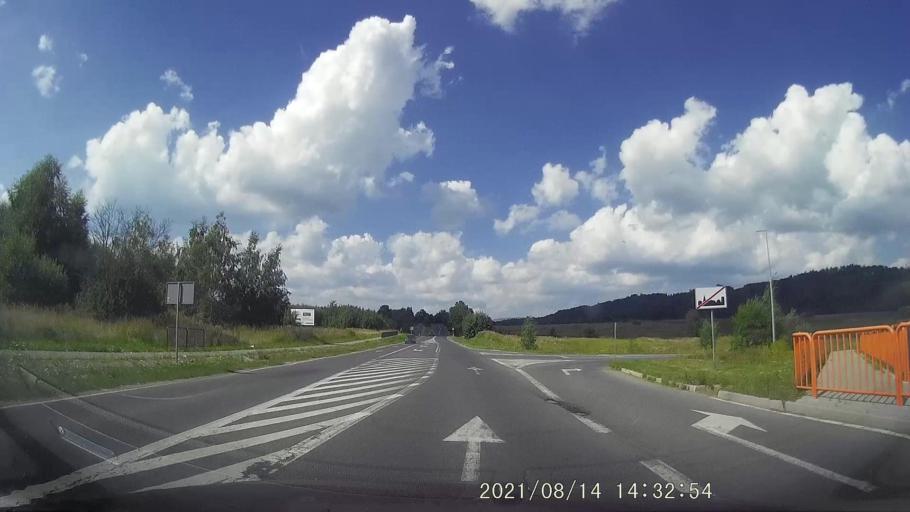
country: PL
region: Lower Silesian Voivodeship
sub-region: Powiat klodzki
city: Bozkow
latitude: 50.5536
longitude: 16.5474
